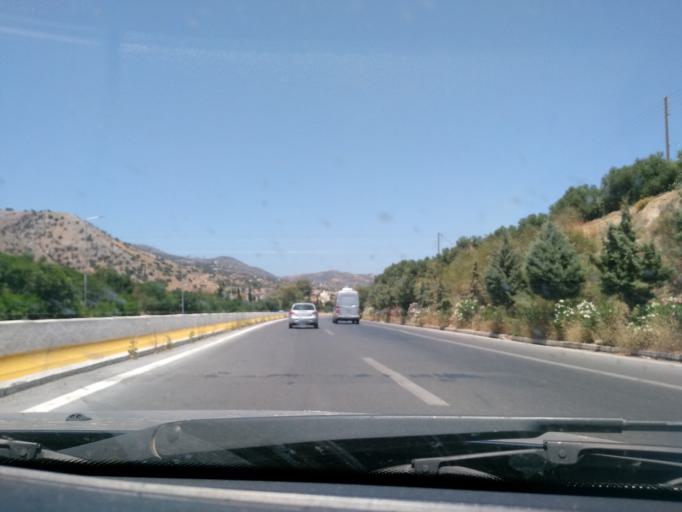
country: GR
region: Crete
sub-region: Nomos Irakleiou
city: Gazi
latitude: 35.3286
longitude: 25.0539
